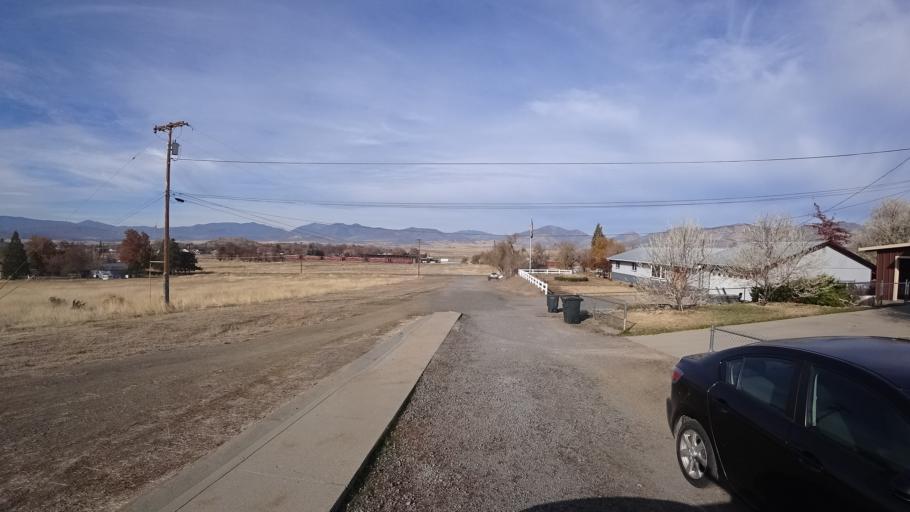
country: US
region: California
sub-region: Siskiyou County
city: Montague
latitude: 41.7313
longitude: -122.5199
